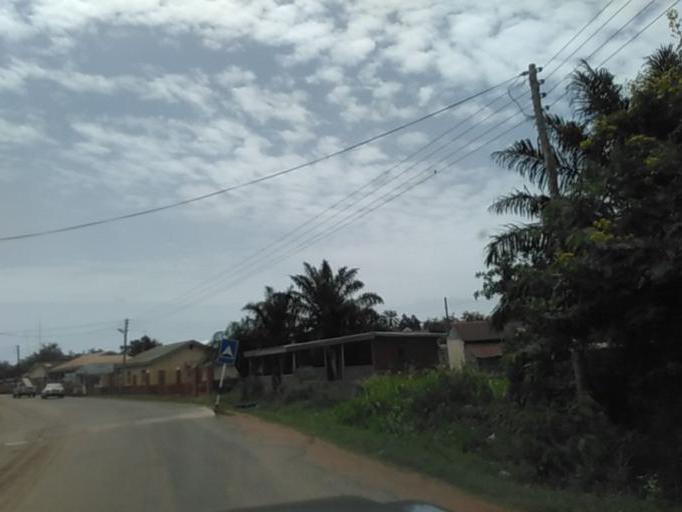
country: GH
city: Akropong
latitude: 6.0977
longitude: 0.1242
